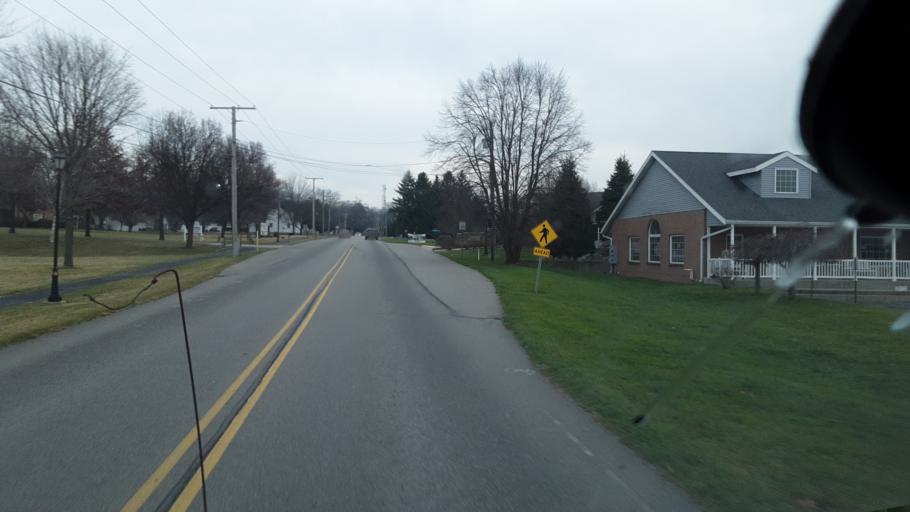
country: US
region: Indiana
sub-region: Elkhart County
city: Middlebury
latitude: 41.6685
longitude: -85.7179
